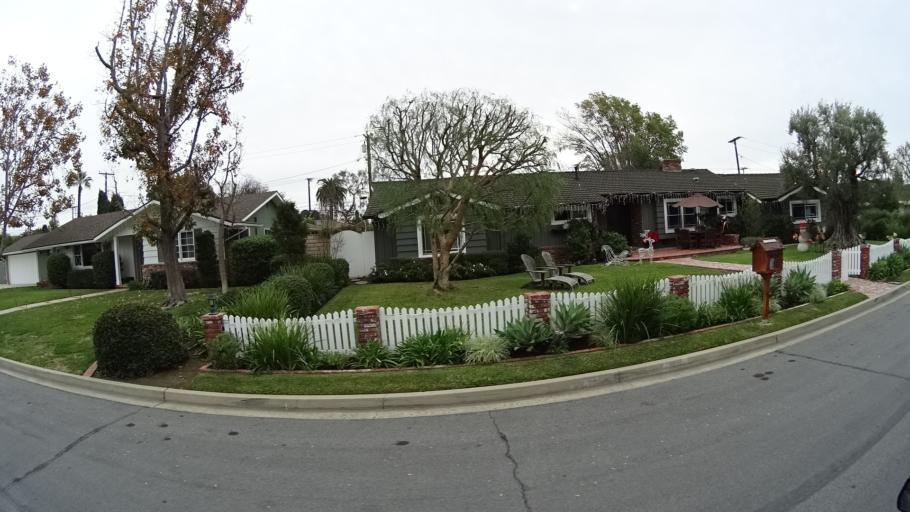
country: US
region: California
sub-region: Orange County
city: North Tustin
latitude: 33.7421
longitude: -117.7968
